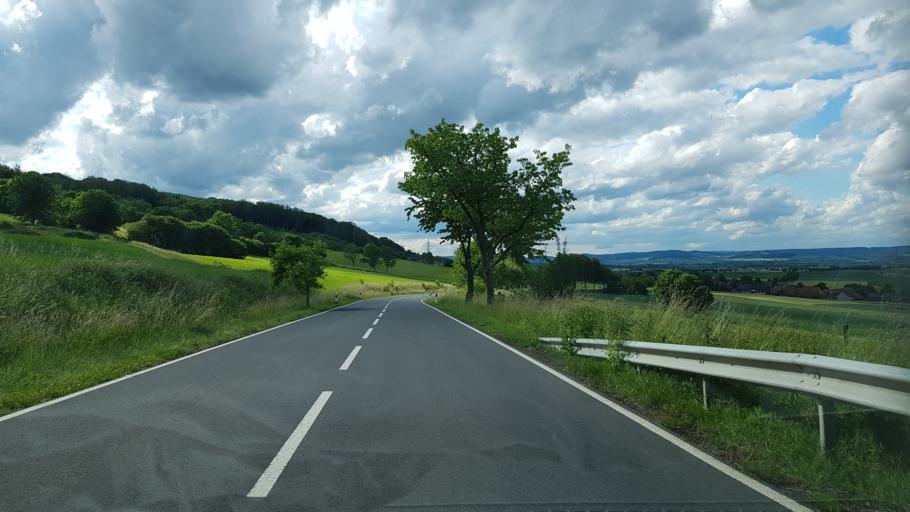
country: DE
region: Lower Saxony
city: Moringen
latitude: 51.7334
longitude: 9.8876
